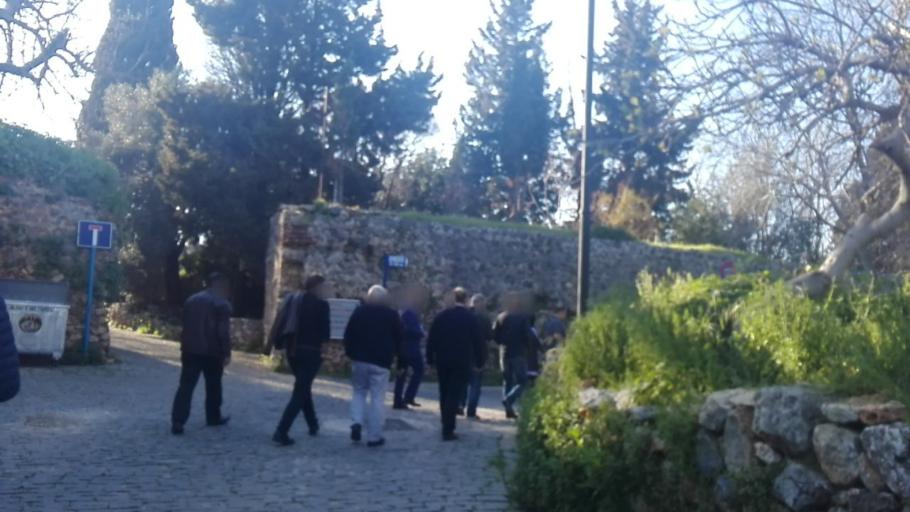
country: TR
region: Antalya
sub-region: Alanya
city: Alanya
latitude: 36.5340
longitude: 31.9932
